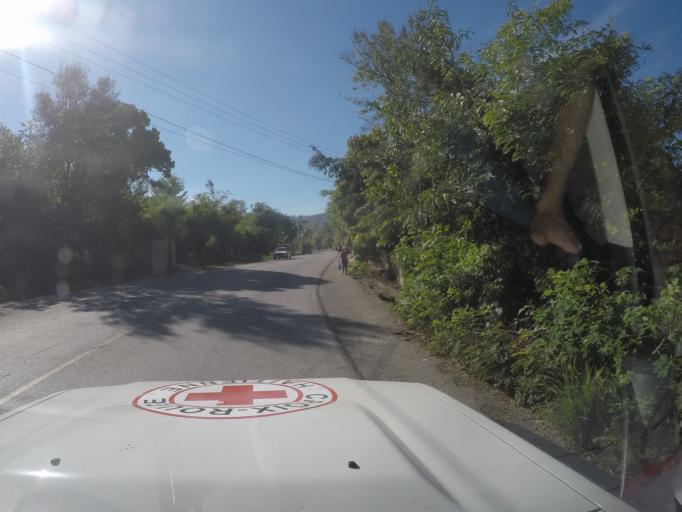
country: HT
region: Ouest
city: Leogane
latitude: 18.4515
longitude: -72.6596
